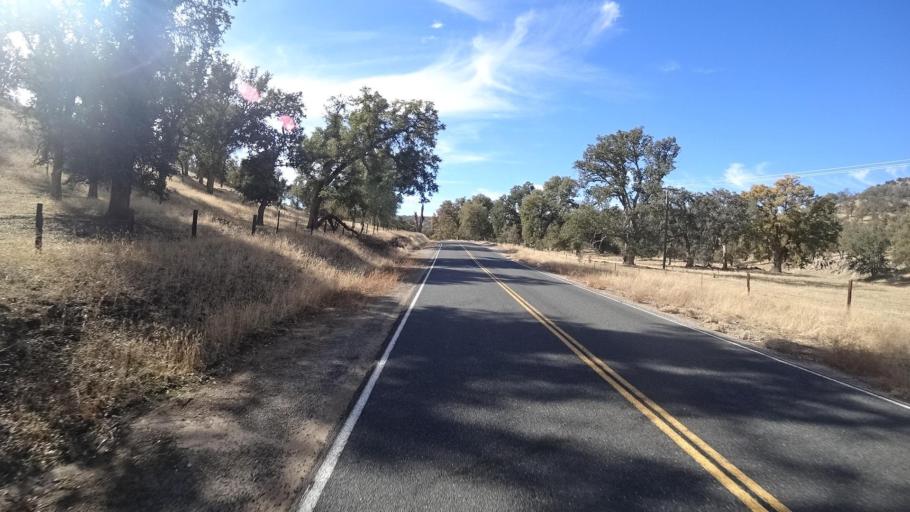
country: US
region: California
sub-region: Kern County
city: Alta Sierra
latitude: 35.6689
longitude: -118.7442
